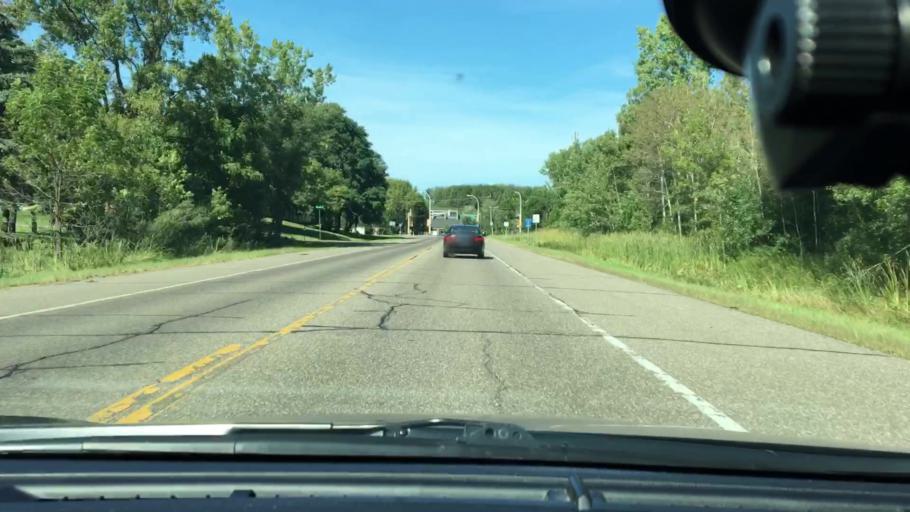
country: US
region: Minnesota
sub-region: Washington County
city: Mahtomedi
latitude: 45.0550
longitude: -92.9475
